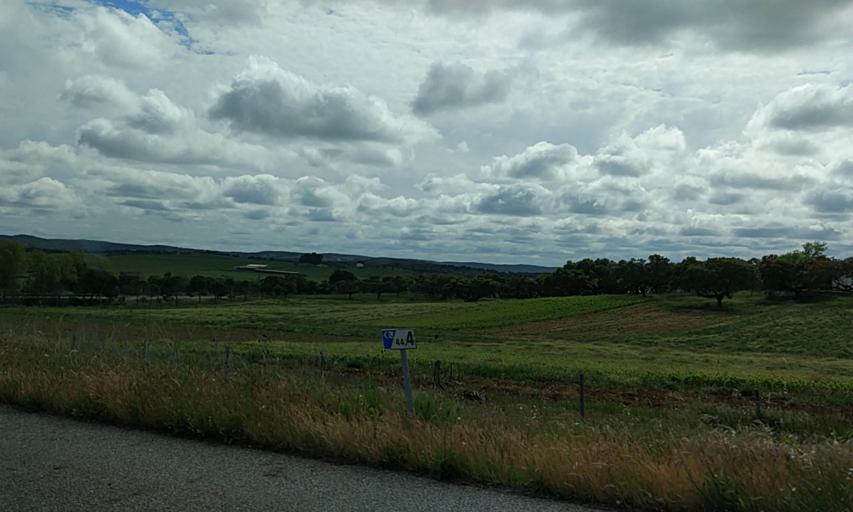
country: PT
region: Evora
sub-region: Montemor-O-Novo
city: Montemor-o-Novo
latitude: 38.6612
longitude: -8.1704
